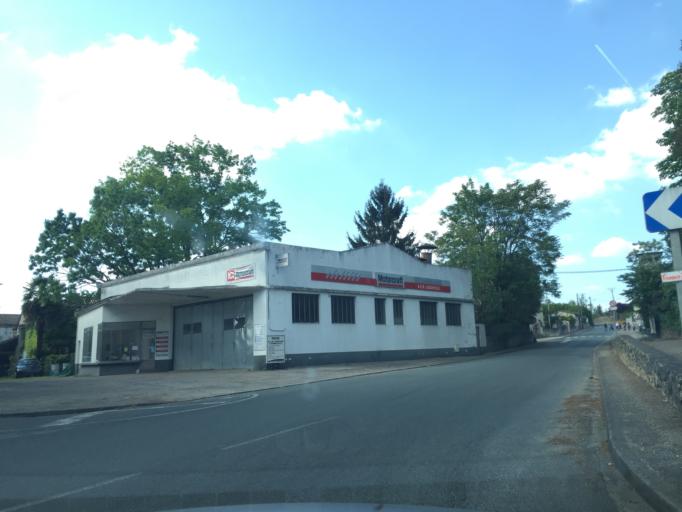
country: FR
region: Aquitaine
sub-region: Departement de la Gironde
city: Sauveterre-de-Guyenne
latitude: 44.6912
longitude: -0.0843
